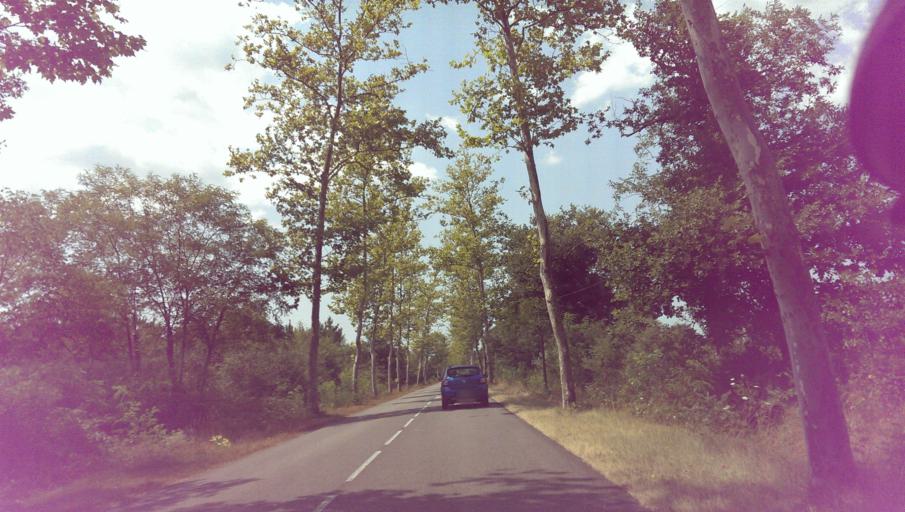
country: FR
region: Aquitaine
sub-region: Departement des Landes
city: Sabres
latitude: 44.1264
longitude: -0.6882
